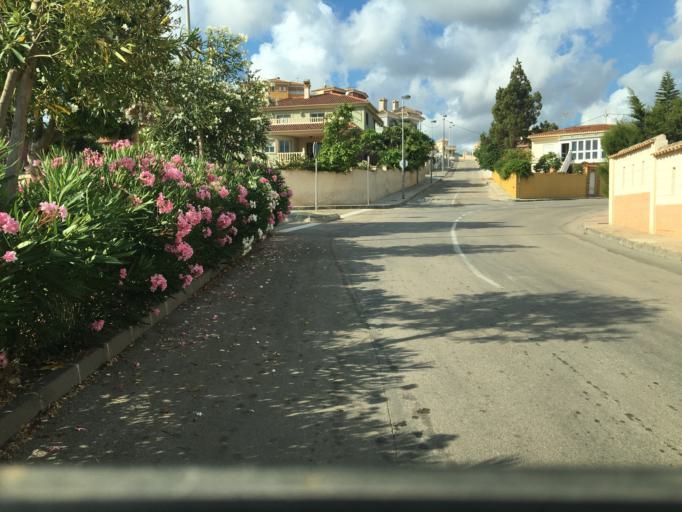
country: ES
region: Murcia
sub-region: Murcia
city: Los Alcazares
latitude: 37.6936
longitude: -0.8431
